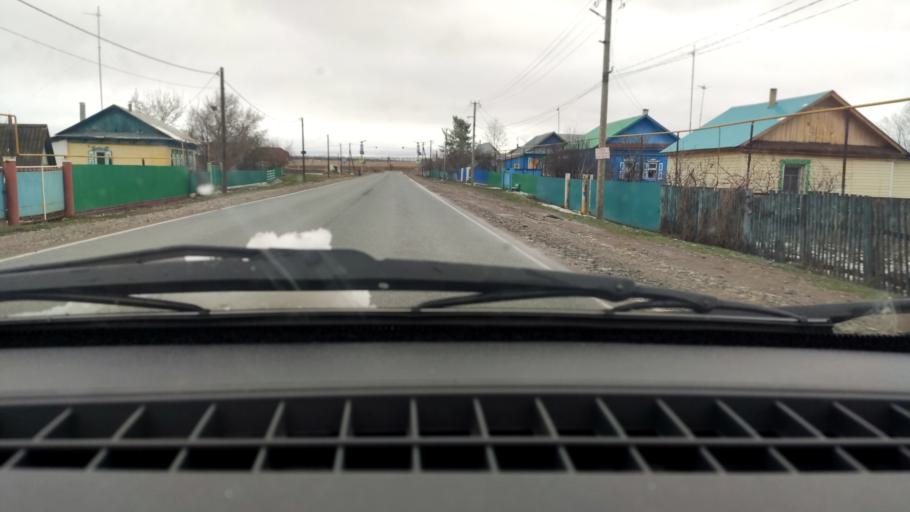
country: RU
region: Bashkortostan
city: Alekseyevka
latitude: 55.0744
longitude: 55.0813
